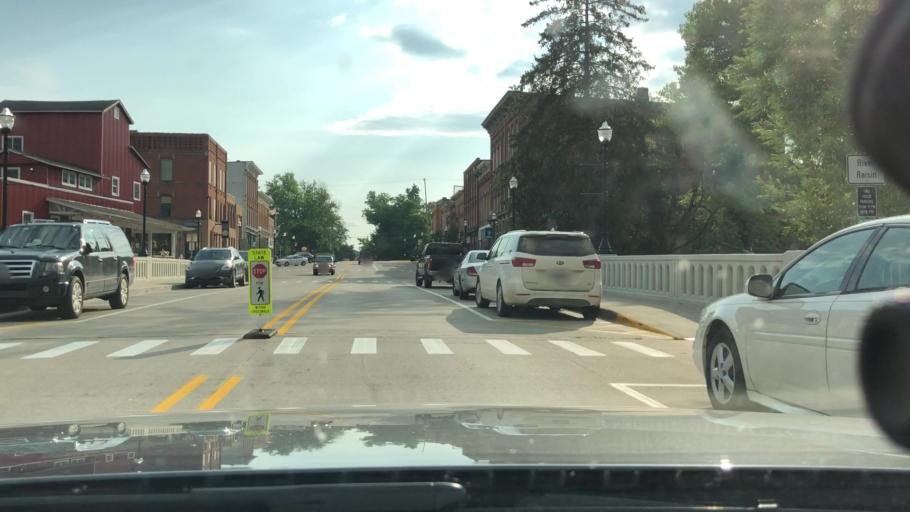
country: US
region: Michigan
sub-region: Washtenaw County
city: Manchester
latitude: 42.1502
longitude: -84.0381
